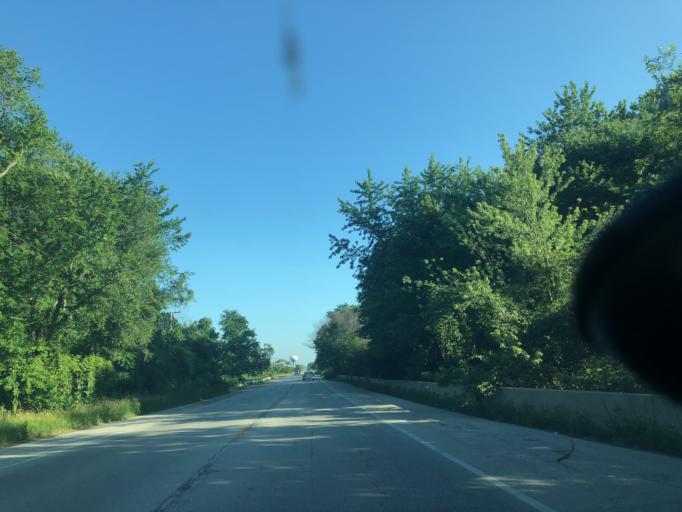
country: US
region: Illinois
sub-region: Cook County
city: Orland Hills
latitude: 41.5838
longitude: -87.8910
